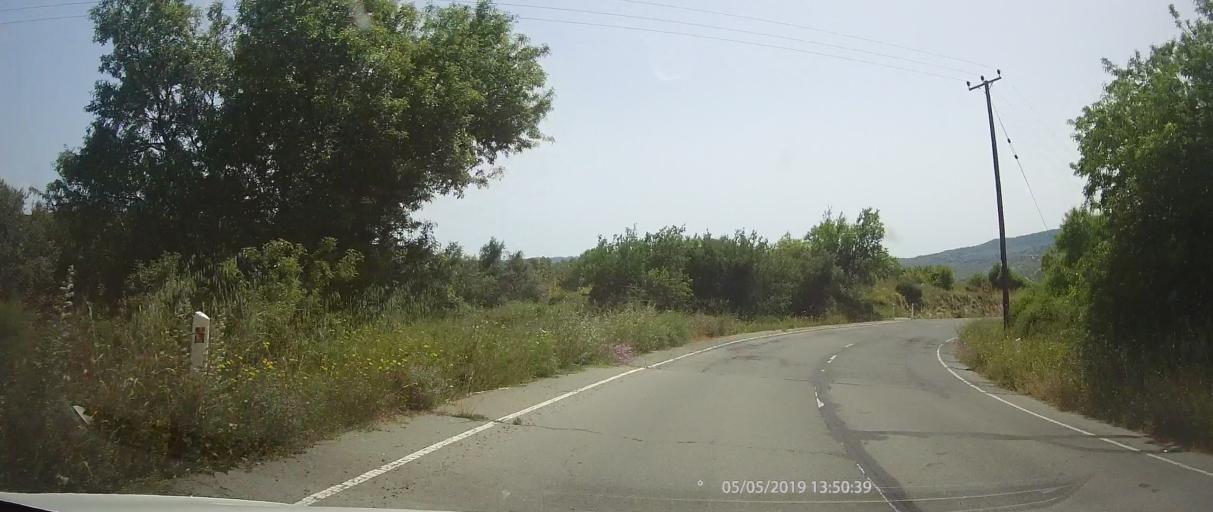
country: CY
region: Limassol
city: Pachna
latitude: 34.8406
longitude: 32.7377
